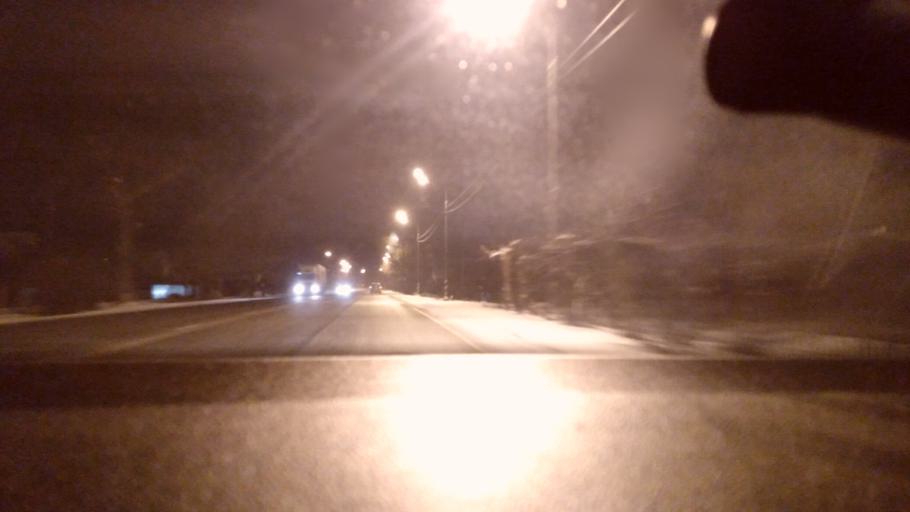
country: RU
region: Moskovskaya
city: Voskresensk
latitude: 55.1972
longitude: 38.6161
